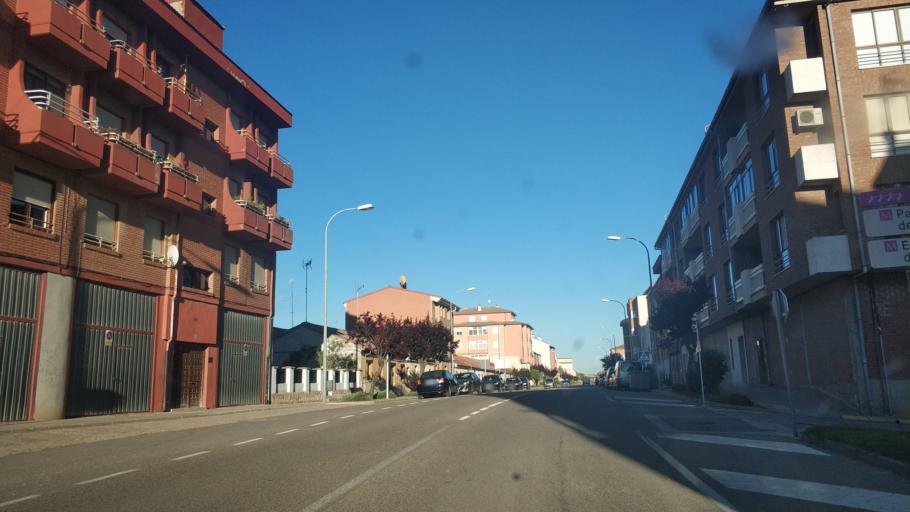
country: ES
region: Castille and Leon
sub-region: Provincia de Soria
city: San Esteban de Gormaz
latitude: 41.5726
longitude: -3.1997
